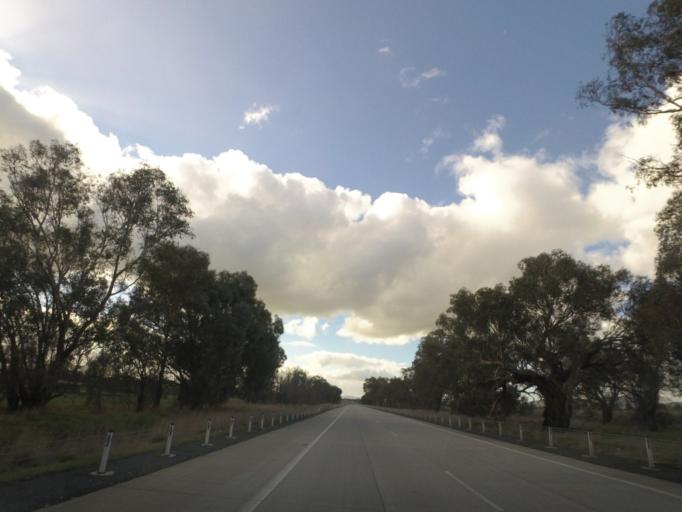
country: AU
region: New South Wales
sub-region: Greater Hume Shire
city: Holbrook
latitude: -35.7433
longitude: 147.3013
